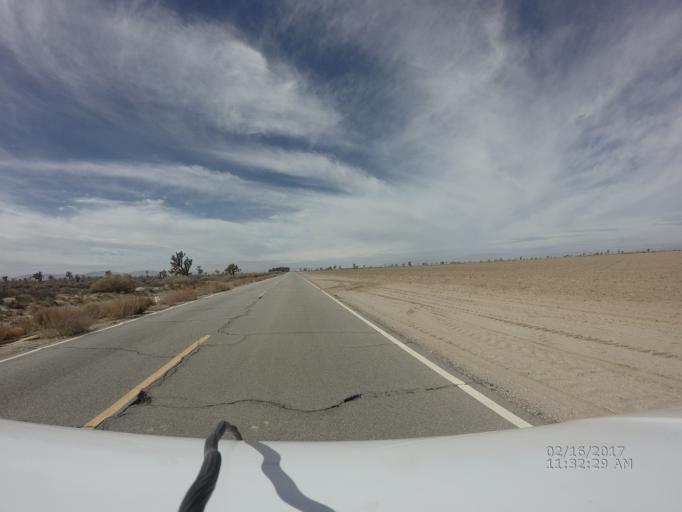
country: US
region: California
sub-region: Los Angeles County
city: Lake Los Angeles
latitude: 34.7047
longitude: -117.9486
